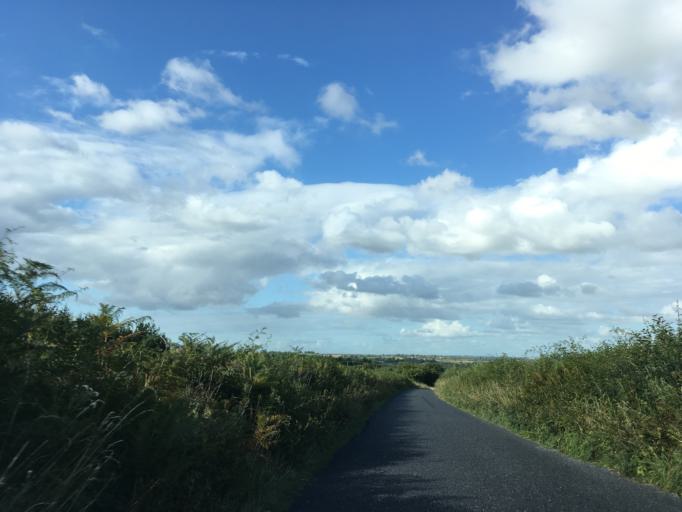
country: IE
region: Munster
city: Cahir
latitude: 52.2672
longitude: -7.9584
